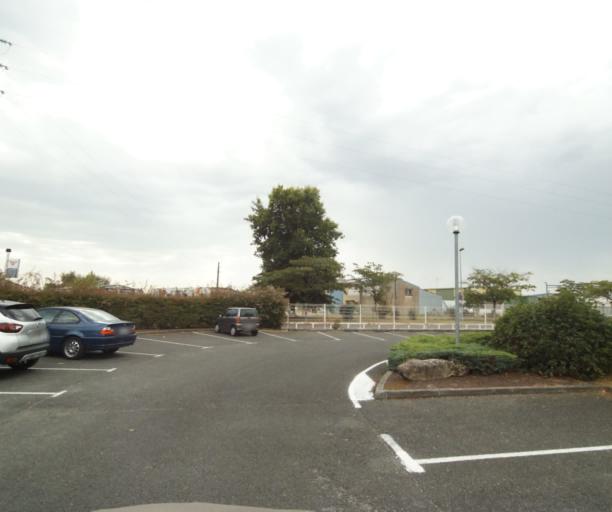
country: FR
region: Aquitaine
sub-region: Departement de la Gironde
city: Creon
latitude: 44.7711
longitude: -0.3358
